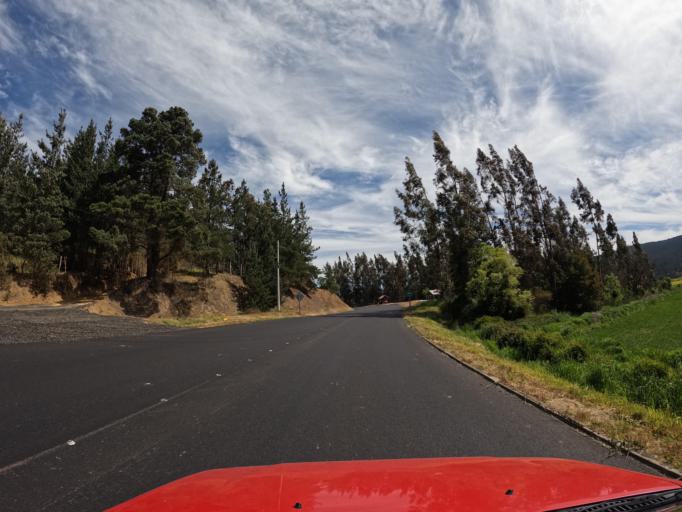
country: CL
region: Maule
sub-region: Provincia de Talca
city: Constitucion
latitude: -35.0614
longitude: -72.0379
